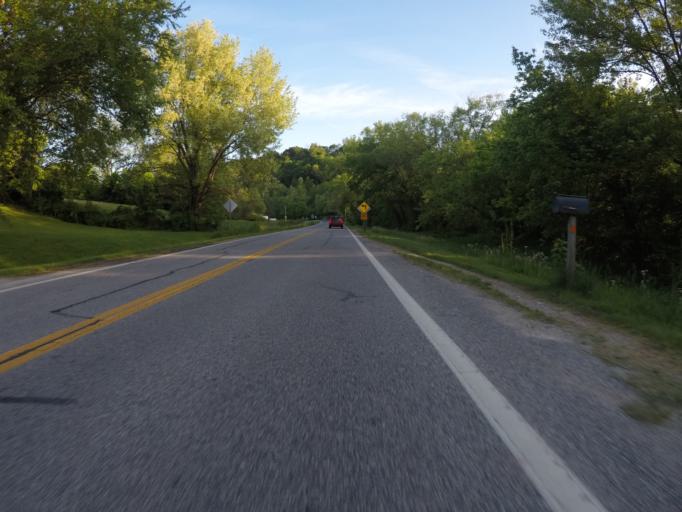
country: US
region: West Virginia
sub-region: Cabell County
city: Huntington
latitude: 38.4929
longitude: -82.4770
